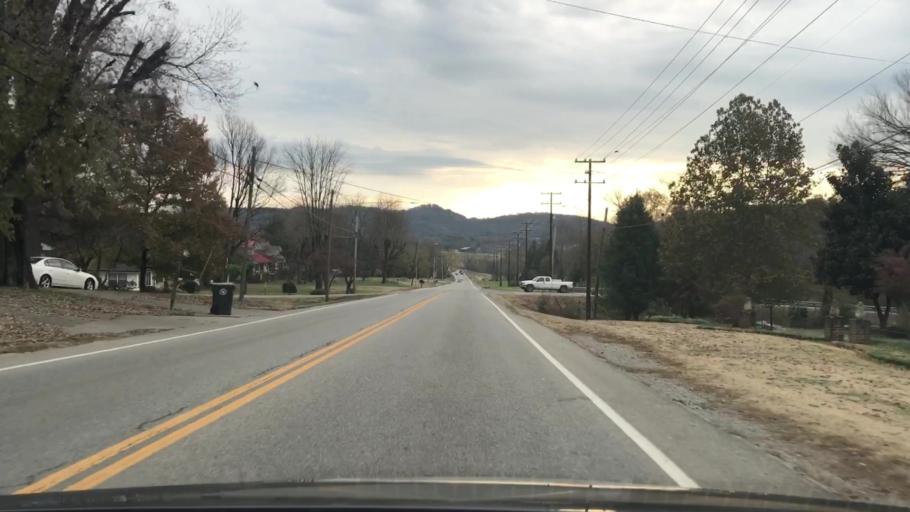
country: US
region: Tennessee
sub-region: Trousdale County
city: Hartsville
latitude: 36.3871
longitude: -86.1370
